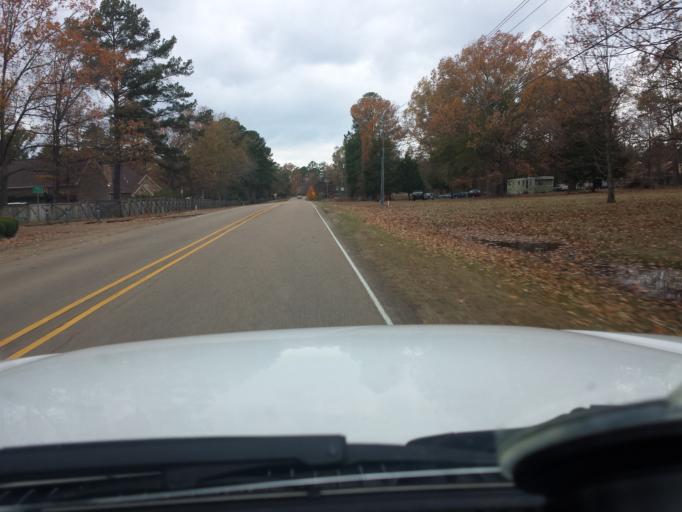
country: US
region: Mississippi
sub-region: Madison County
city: Madison
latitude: 32.4136
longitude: -90.0150
